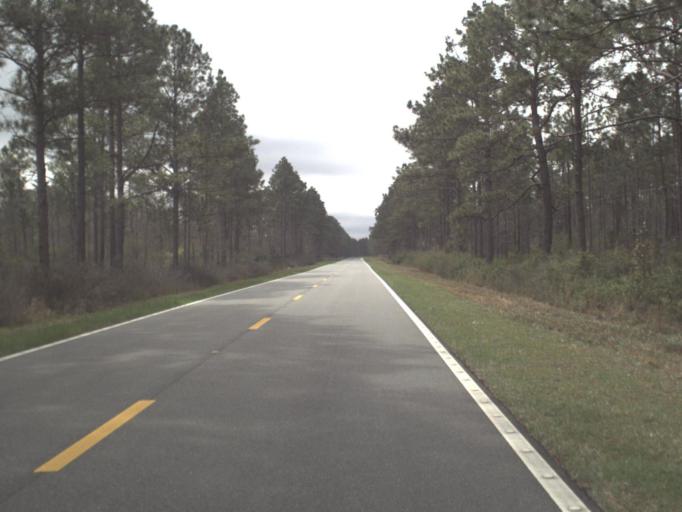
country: US
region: Florida
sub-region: Gulf County
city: Wewahitchka
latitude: 30.0924
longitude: -84.9845
